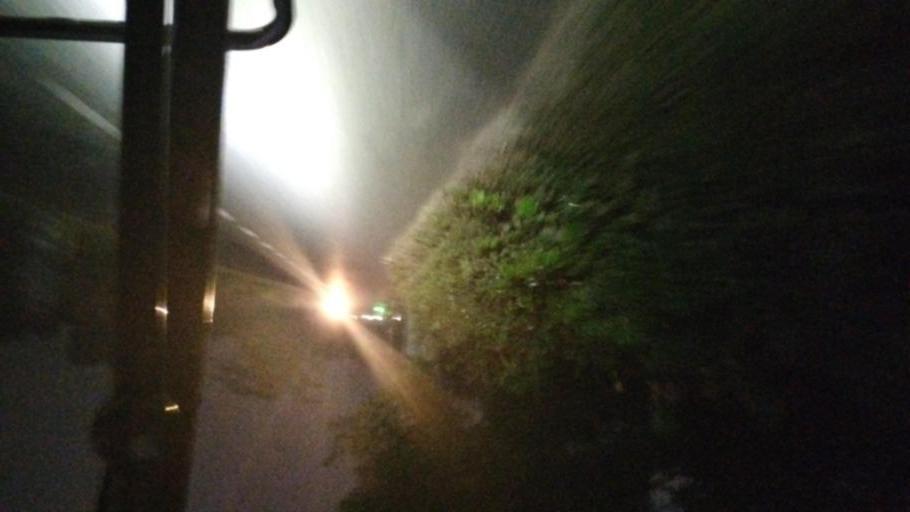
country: BD
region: Dhaka
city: Gafargaon
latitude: 24.4000
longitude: 90.3664
